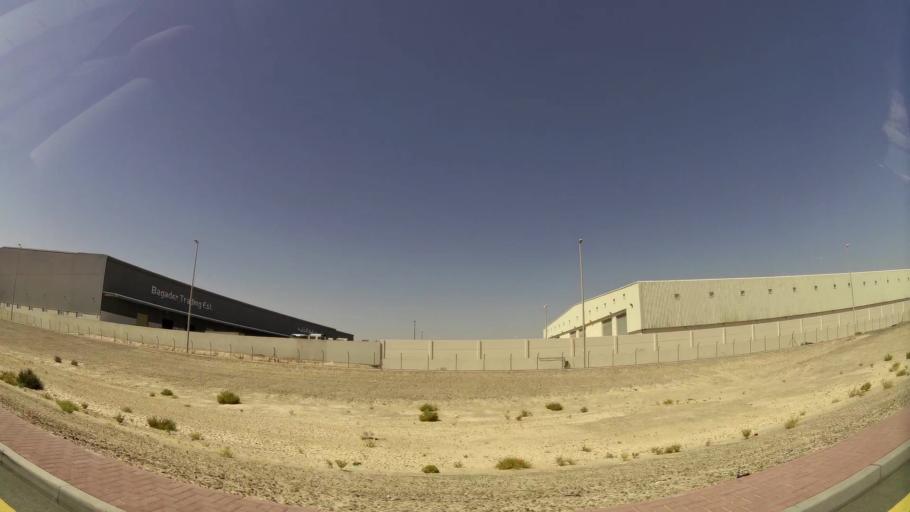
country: AE
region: Dubai
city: Dubai
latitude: 24.9614
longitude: 55.1193
